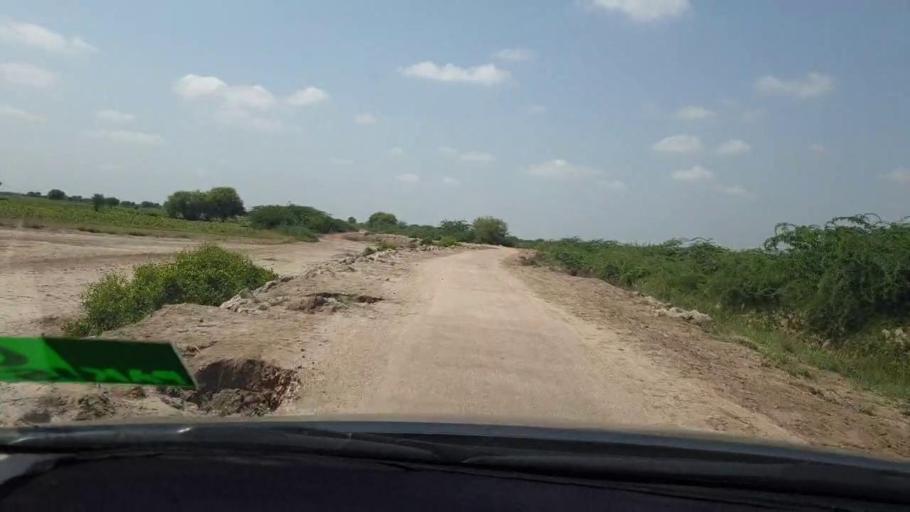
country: PK
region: Sindh
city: Naukot
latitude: 24.8851
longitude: 69.2103
